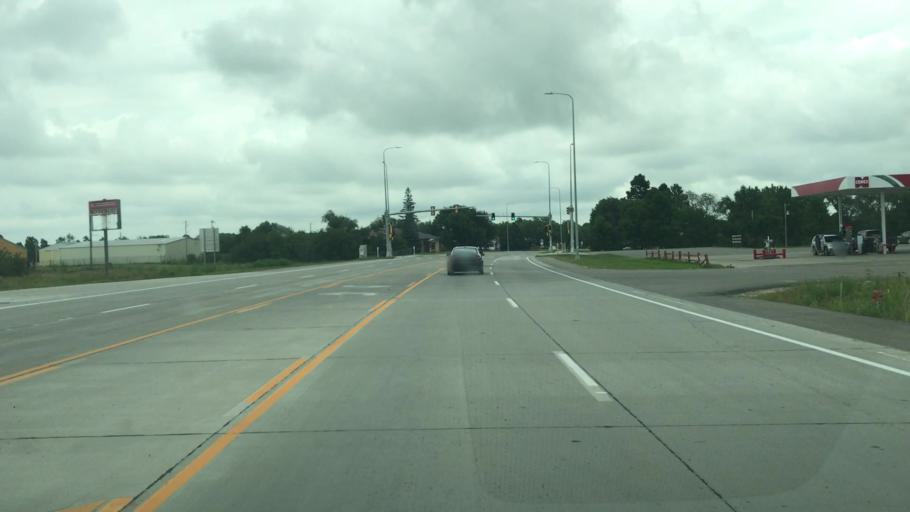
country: US
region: South Dakota
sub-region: Todd County
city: Mission
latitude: 43.3053
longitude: -100.6694
